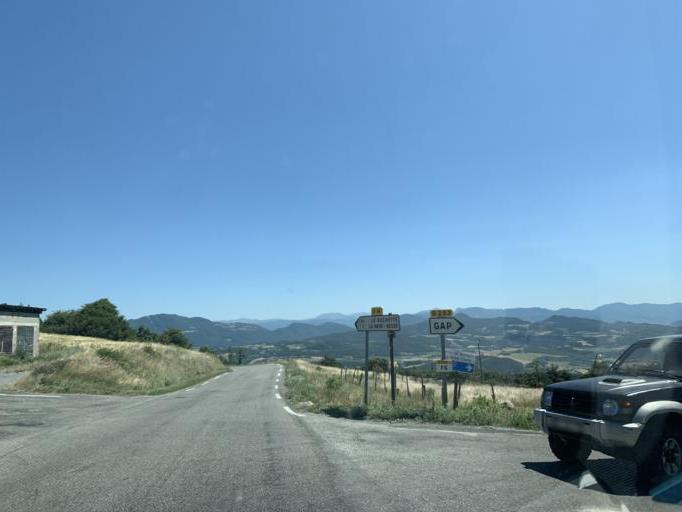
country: FR
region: Provence-Alpes-Cote d'Azur
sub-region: Departement des Hautes-Alpes
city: La Batie-Neuve
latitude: 44.6042
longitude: 6.1423
